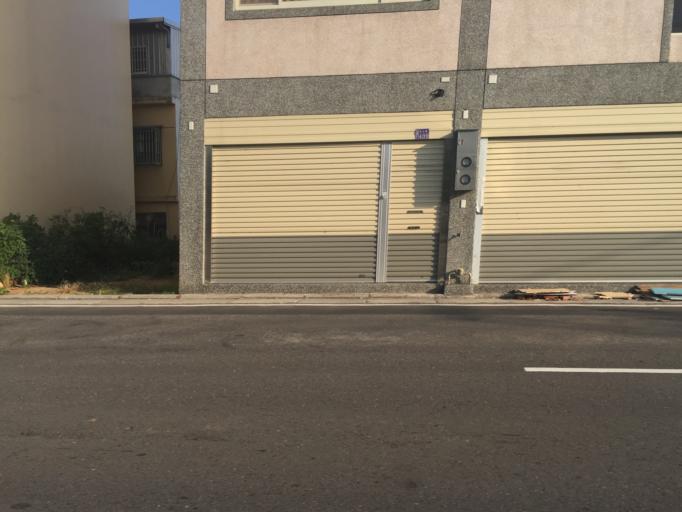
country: TW
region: Taiwan
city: Daxi
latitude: 24.9244
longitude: 121.2575
